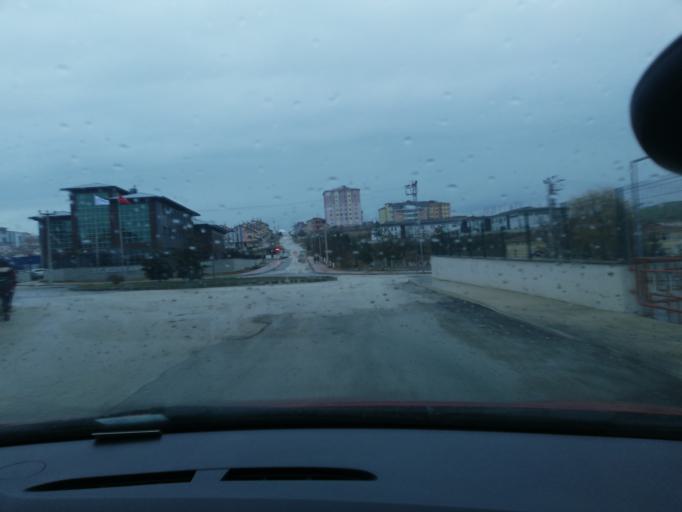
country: TR
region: Kastamonu
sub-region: Cide
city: Kastamonu
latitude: 41.4236
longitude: 33.8001
